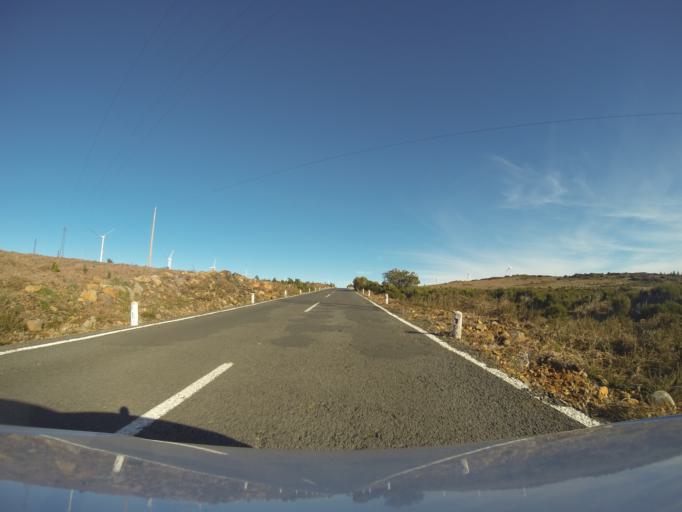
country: PT
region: Madeira
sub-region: Sao Vicente
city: Sao Vicente
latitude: 32.7641
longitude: -17.0719
